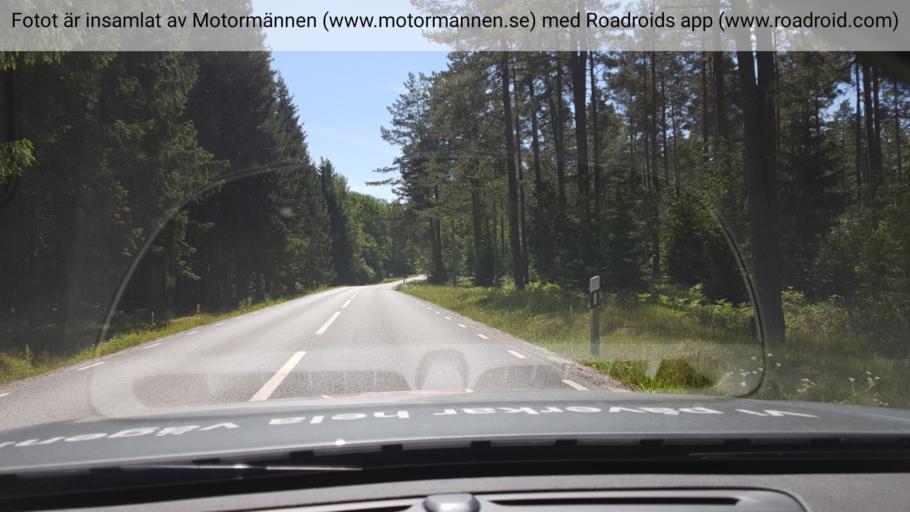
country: SE
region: Stockholm
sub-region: Haninge Kommun
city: Haninge
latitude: 59.1465
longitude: 18.1811
